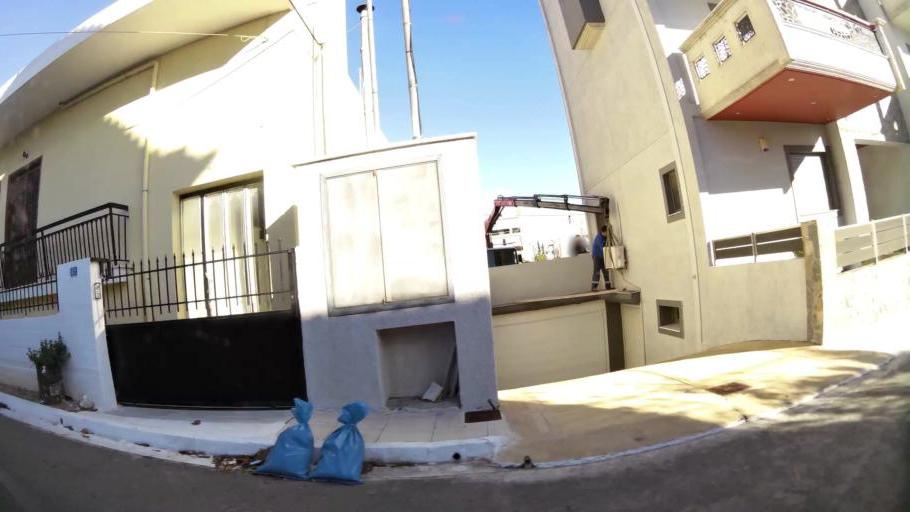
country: GR
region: Attica
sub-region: Nomarchia Anatolikis Attikis
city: Acharnes
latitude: 38.0974
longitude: 23.7290
